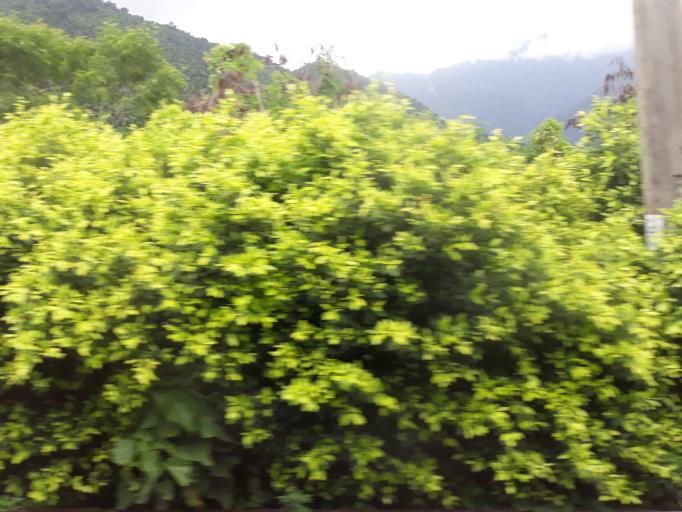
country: TW
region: Taiwan
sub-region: Yilan
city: Yilan
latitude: 24.4386
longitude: 121.7808
